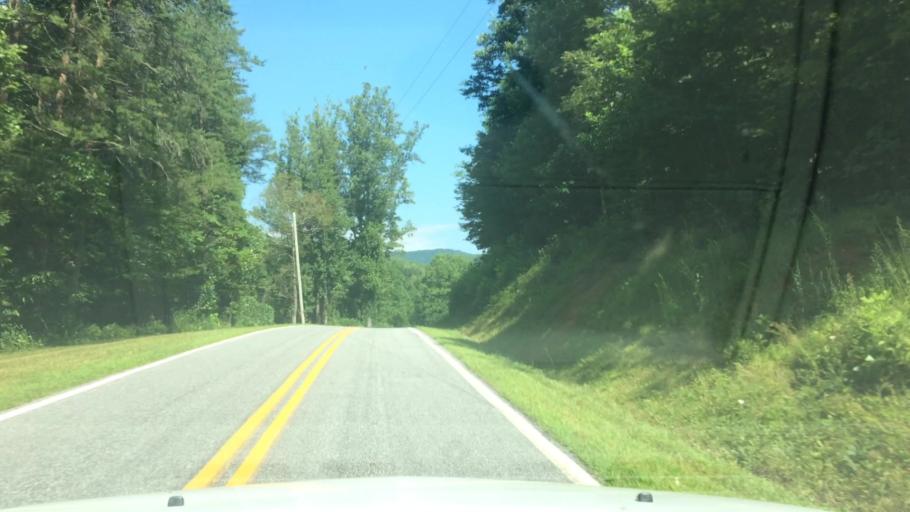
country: US
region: North Carolina
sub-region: Alexander County
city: Taylorsville
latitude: 35.9762
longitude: -81.2752
